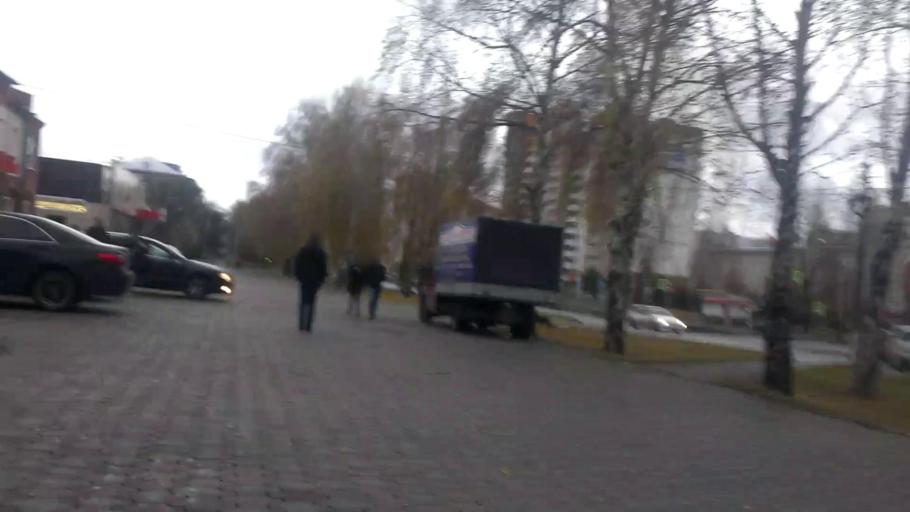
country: RU
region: Altai Krai
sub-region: Gorod Barnaulskiy
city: Barnaul
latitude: 53.3610
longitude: 83.6895
